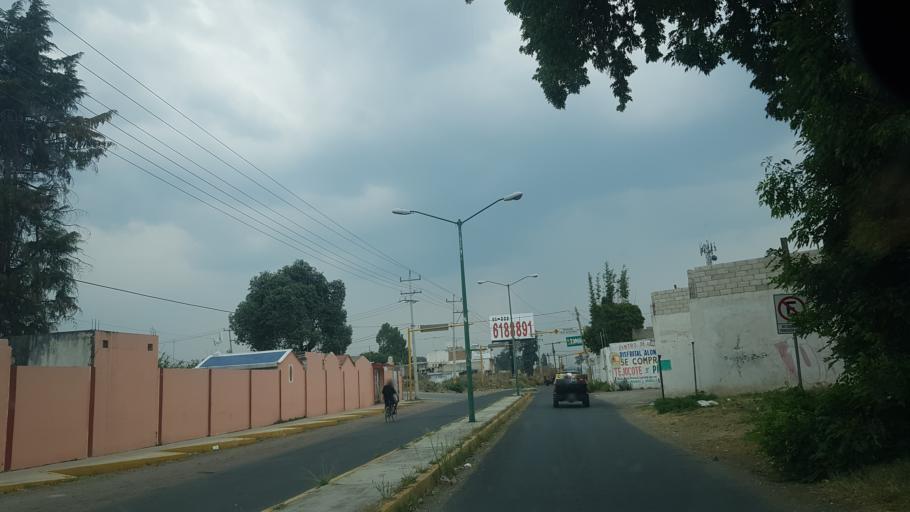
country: MX
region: Puebla
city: Huejotzingo
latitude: 19.1692
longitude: -98.4117
